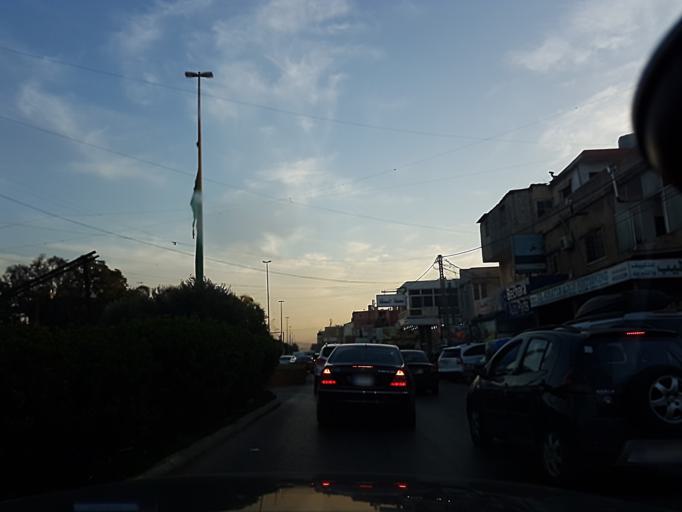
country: LB
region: Beyrouth
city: Beirut
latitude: 33.8388
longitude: 35.4847
